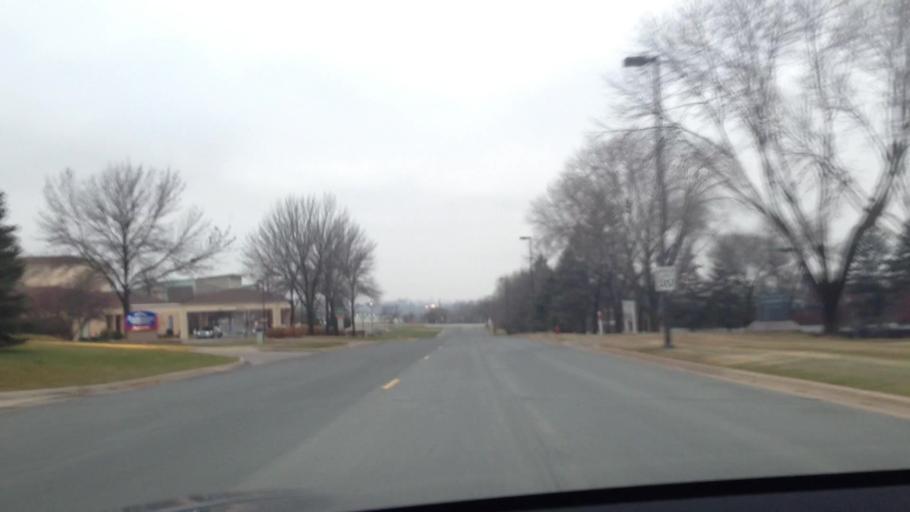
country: US
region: Minnesota
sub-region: Dakota County
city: Mendota Heights
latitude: 44.8636
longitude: -93.1625
